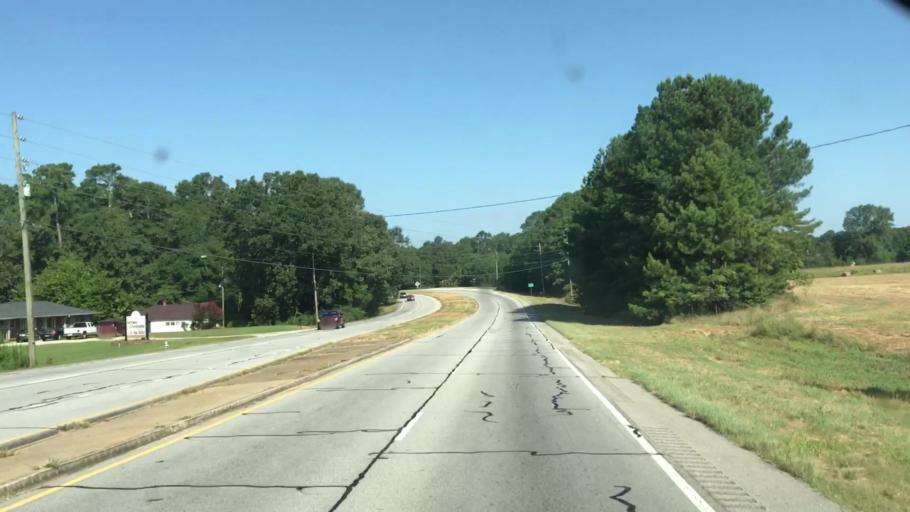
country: US
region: Georgia
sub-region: Walton County
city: Walnut Grove
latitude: 33.8184
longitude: -83.8082
